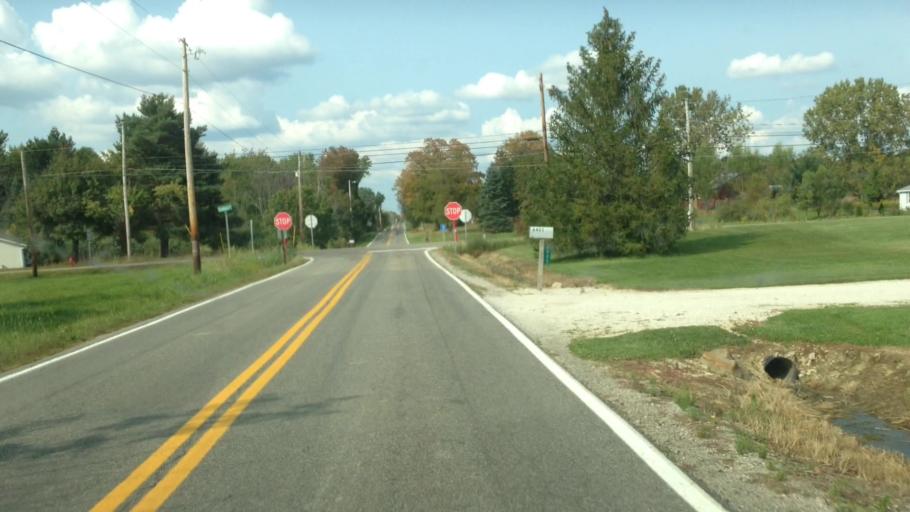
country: US
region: Ohio
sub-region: Medina County
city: Lodi
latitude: 41.0984
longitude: -82.0037
